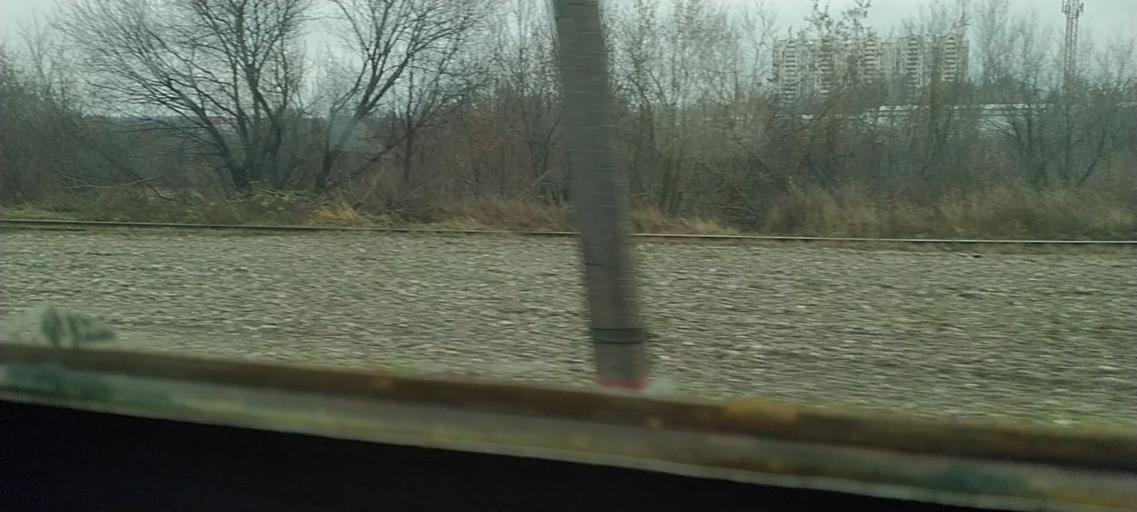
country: RU
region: Moskovskaya
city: Tomilino
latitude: 55.6712
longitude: 37.9646
